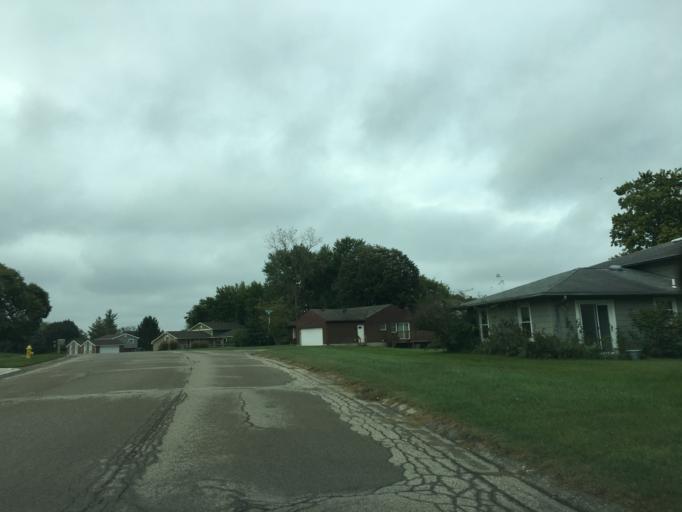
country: US
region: Ohio
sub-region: Butler County
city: Beckett Ridge
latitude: 39.3581
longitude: -84.4465
